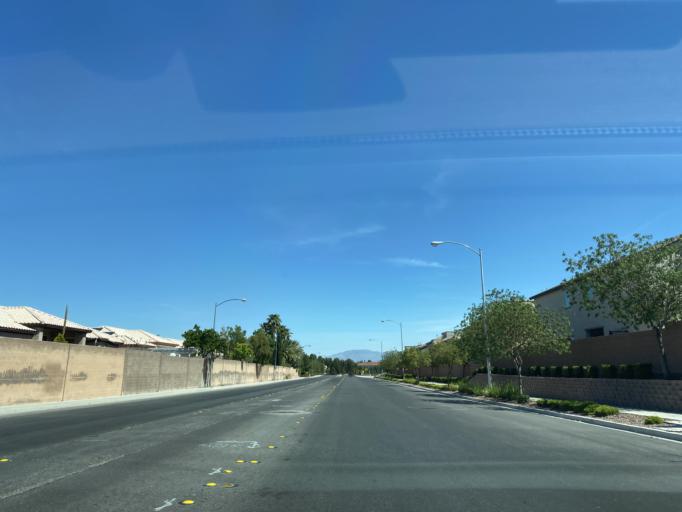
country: US
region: Nevada
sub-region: Clark County
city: Spring Valley
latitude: 36.0887
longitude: -115.2610
